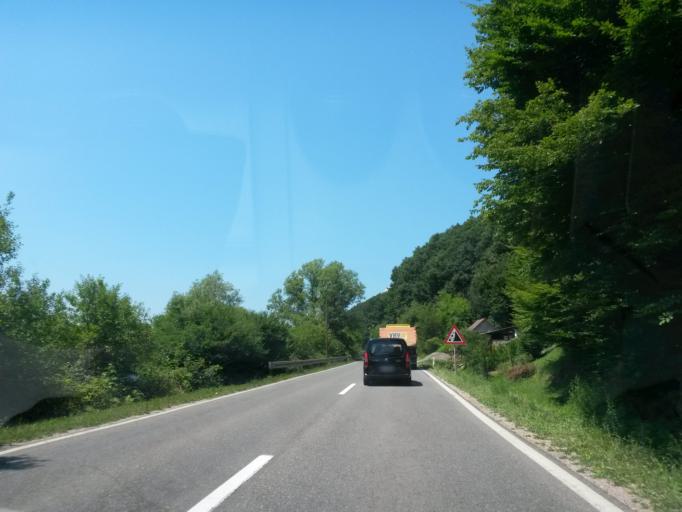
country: BA
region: Federation of Bosnia and Herzegovina
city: Lukavica
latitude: 44.9283
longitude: 18.1818
